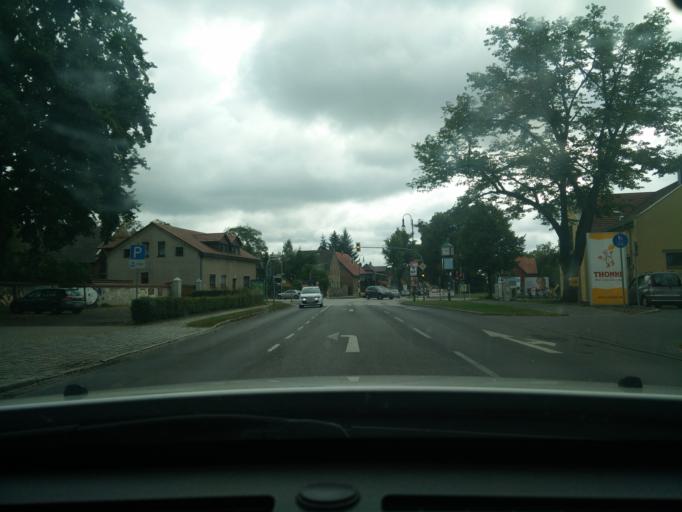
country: DE
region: Brandenburg
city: Falkensee
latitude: 52.5672
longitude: 13.1021
